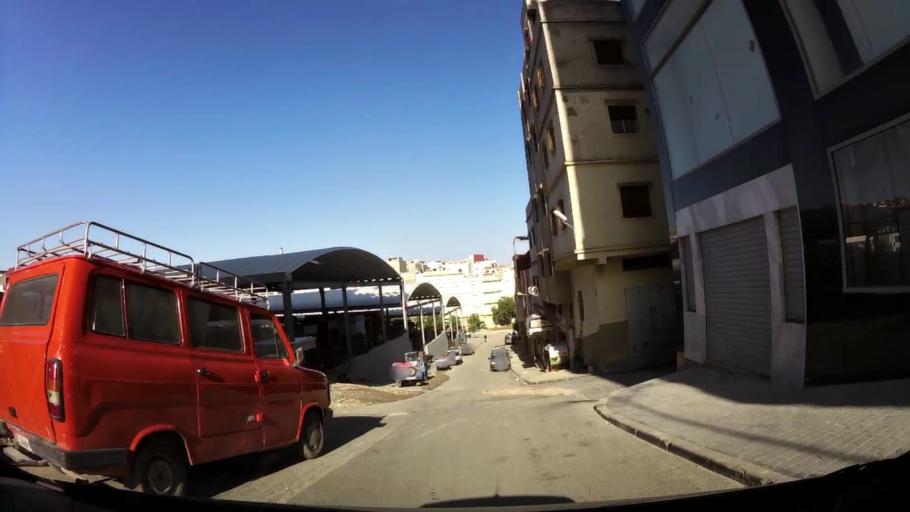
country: MA
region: Tanger-Tetouan
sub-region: Tanger-Assilah
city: Tangier
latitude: 35.7435
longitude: -5.8063
